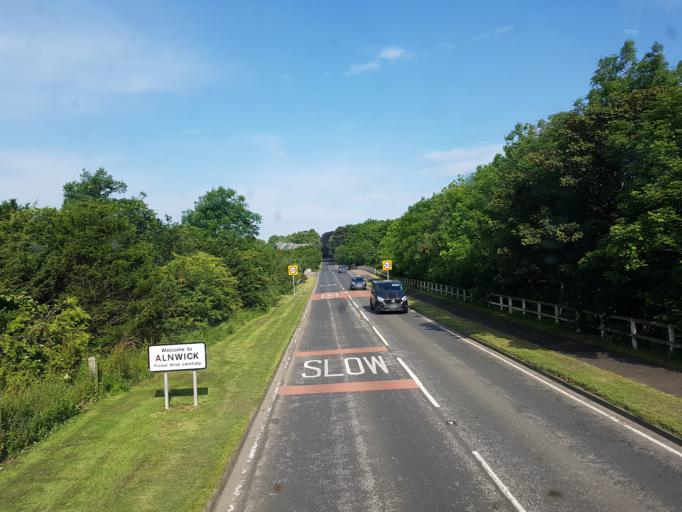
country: GB
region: England
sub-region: Northumberland
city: Alnwick
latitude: 55.4061
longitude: -1.6793
